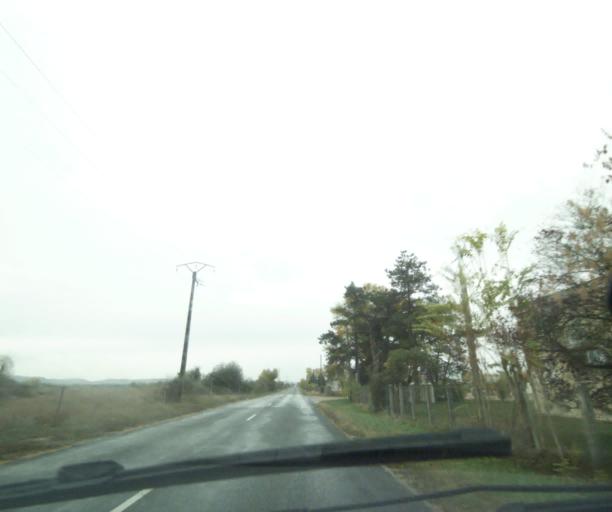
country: FR
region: Rhone-Alpes
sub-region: Departement de l'Ain
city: Saint-Maurice-de-Gourdans
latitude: 45.8094
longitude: 5.2142
